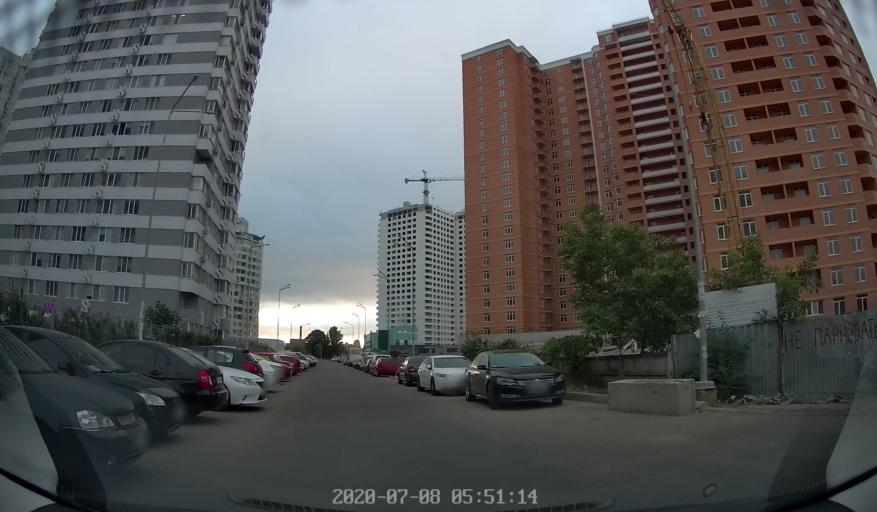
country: TR
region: Kirklareli
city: Sergen
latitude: 41.7799
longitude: 27.6545
